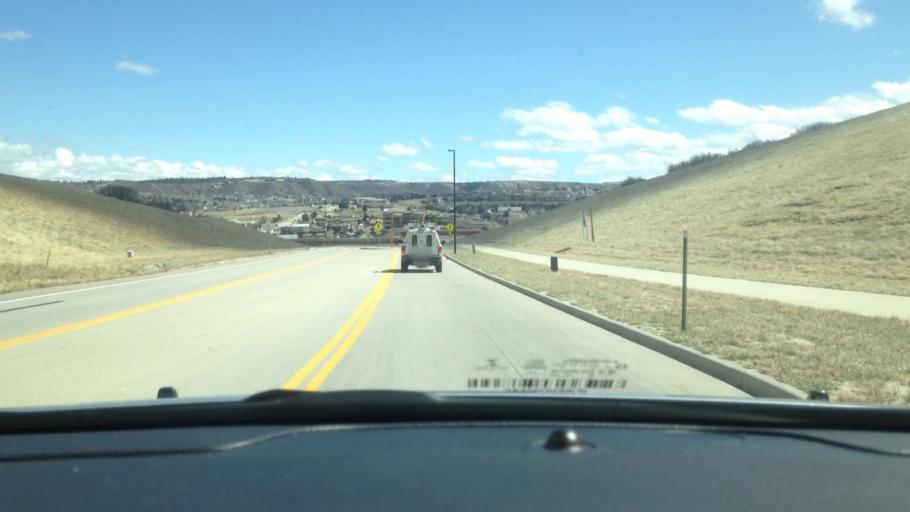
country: US
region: Colorado
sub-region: Douglas County
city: Castle Rock
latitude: 39.3687
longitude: -104.8717
